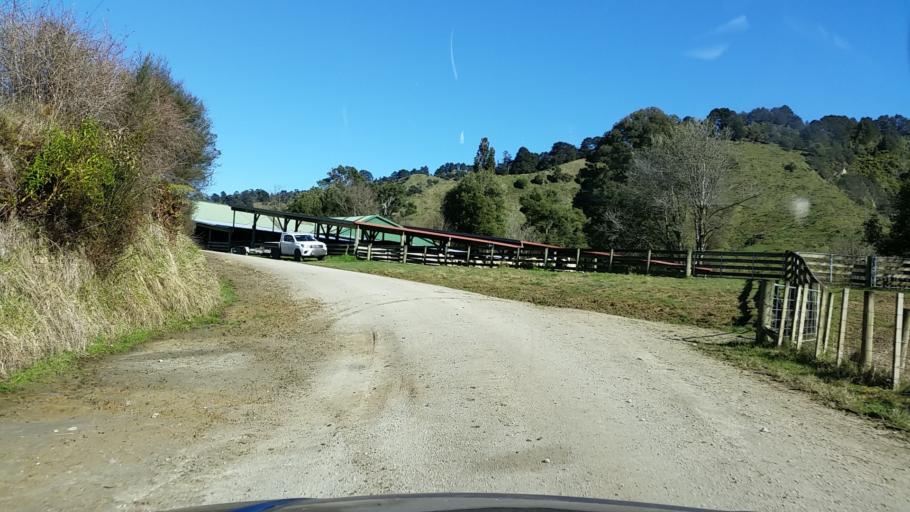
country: NZ
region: Manawatu-Wanganui
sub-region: Wanganui District
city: Wanganui
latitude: -39.5431
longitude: 174.9039
